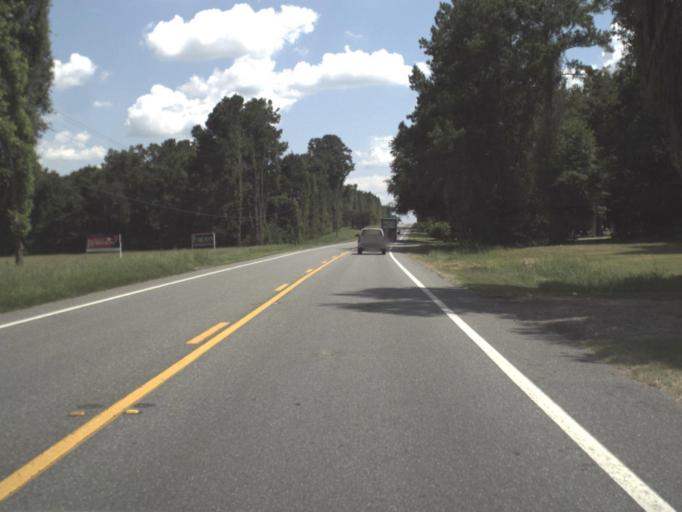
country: US
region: Florida
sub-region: Columbia County
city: Watertown
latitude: 30.0384
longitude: -82.5978
